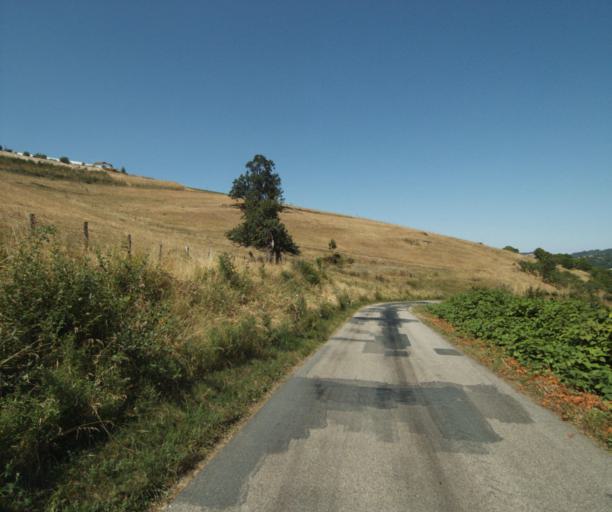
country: FR
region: Rhone-Alpes
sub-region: Departement du Rhone
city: Courzieu
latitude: 45.7280
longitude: 4.5556
